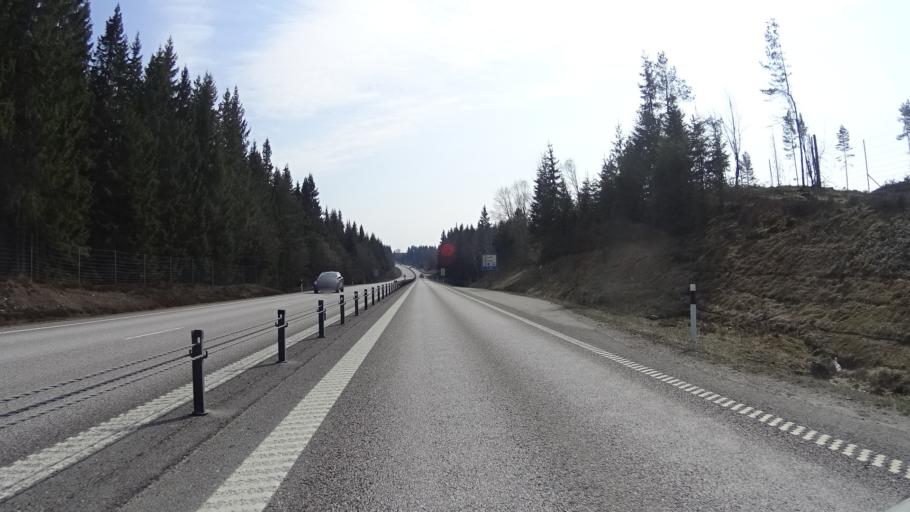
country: SE
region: Vaestra Goetaland
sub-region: Ulricehamns Kommun
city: Ulricehamn
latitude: 57.7853
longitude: 13.6443
